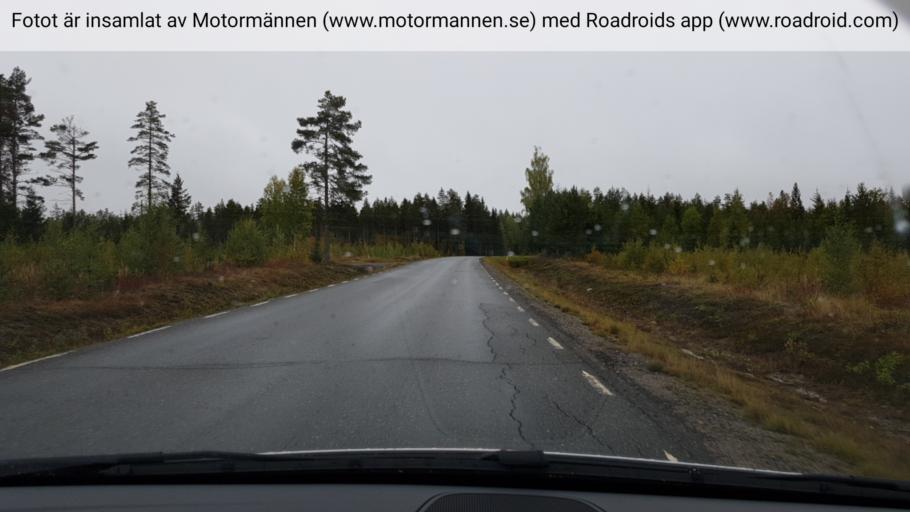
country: SE
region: Vaesterbotten
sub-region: Umea Kommun
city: Ersmark
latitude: 63.9968
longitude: 20.2434
